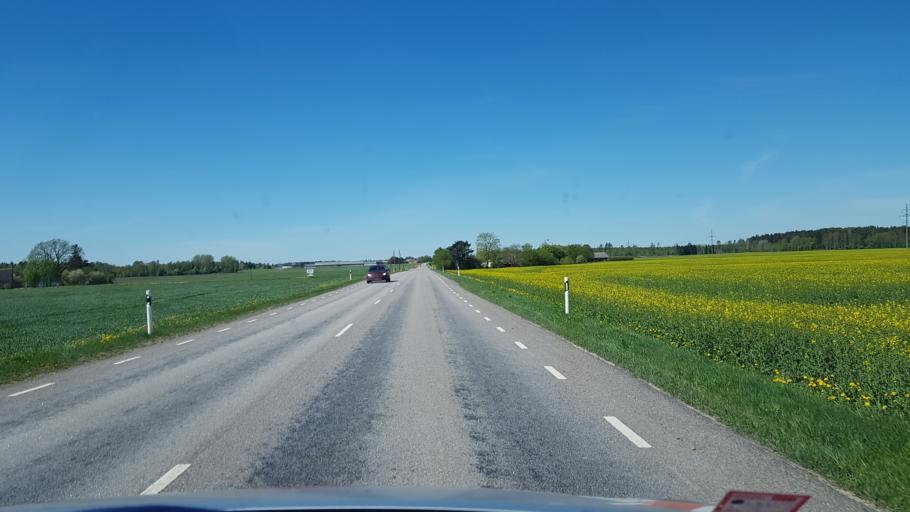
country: EE
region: Tartu
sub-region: Tartu linn
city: Tartu
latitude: 58.3801
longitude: 26.6494
